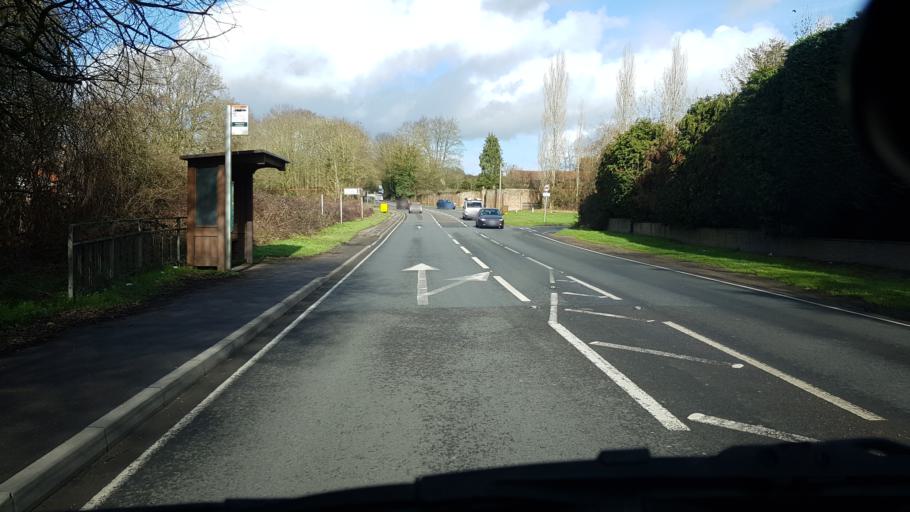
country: GB
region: England
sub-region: Surrey
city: Guildford
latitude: 51.2683
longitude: -0.5759
